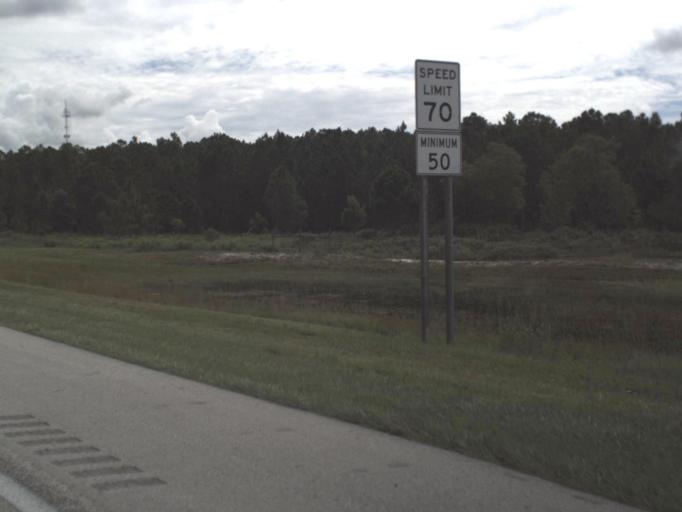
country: US
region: Florida
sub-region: Polk County
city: Polk City
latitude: 28.1753
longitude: -81.7600
